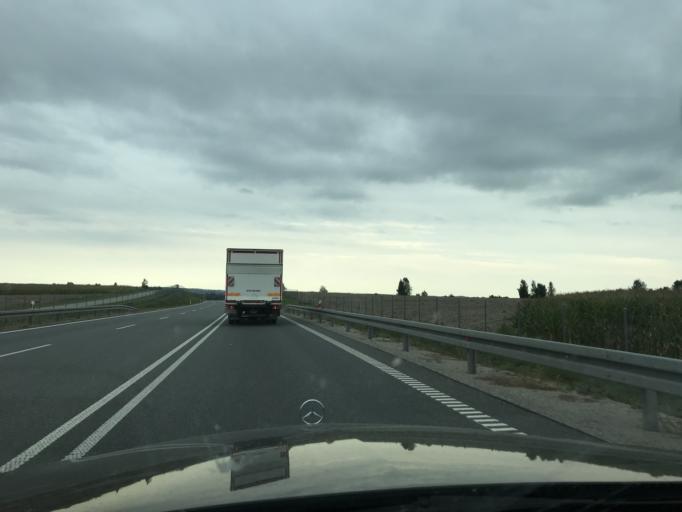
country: PL
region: Subcarpathian Voivodeship
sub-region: Powiat rzeszowski
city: Sokolow Malopolski
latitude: 50.2416
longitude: 22.1378
